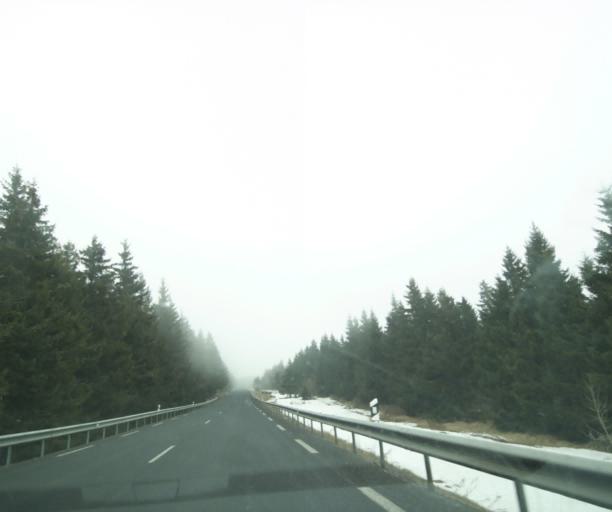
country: FR
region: Languedoc-Roussillon
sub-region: Departement de la Lozere
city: Langogne
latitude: 44.7526
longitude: 3.9440
